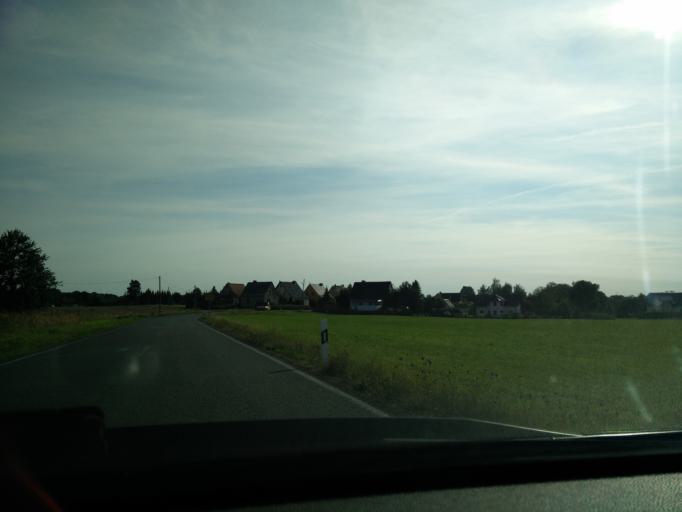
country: DE
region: Saxony
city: Geithain
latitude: 51.0935
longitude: 12.6907
